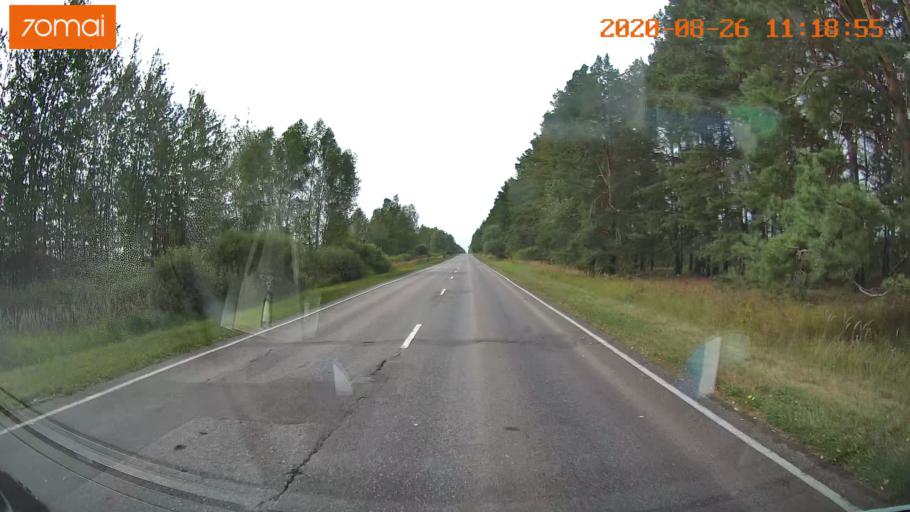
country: RU
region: Rjazan
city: Shilovo
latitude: 54.4051
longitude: 41.0888
